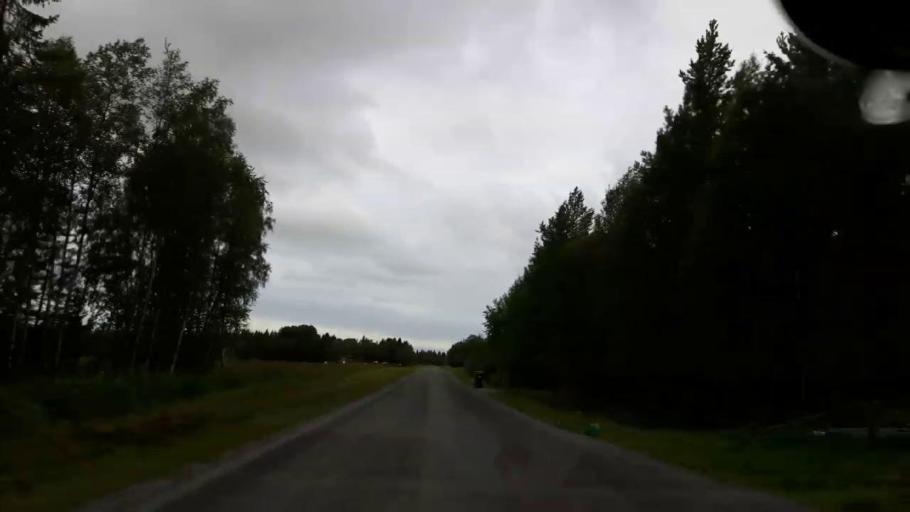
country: SE
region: Jaemtland
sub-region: OEstersunds Kommun
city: Ostersund
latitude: 63.0894
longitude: 14.5548
